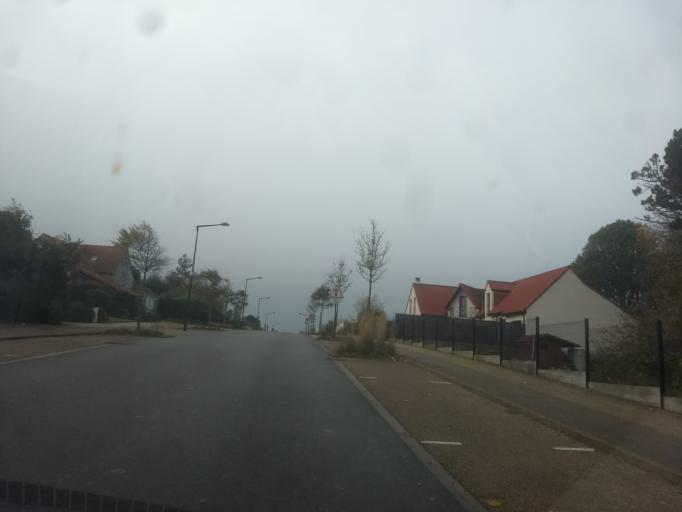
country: FR
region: Nord-Pas-de-Calais
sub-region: Departement du Pas-de-Calais
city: Wissant
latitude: 50.8842
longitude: 1.6652
